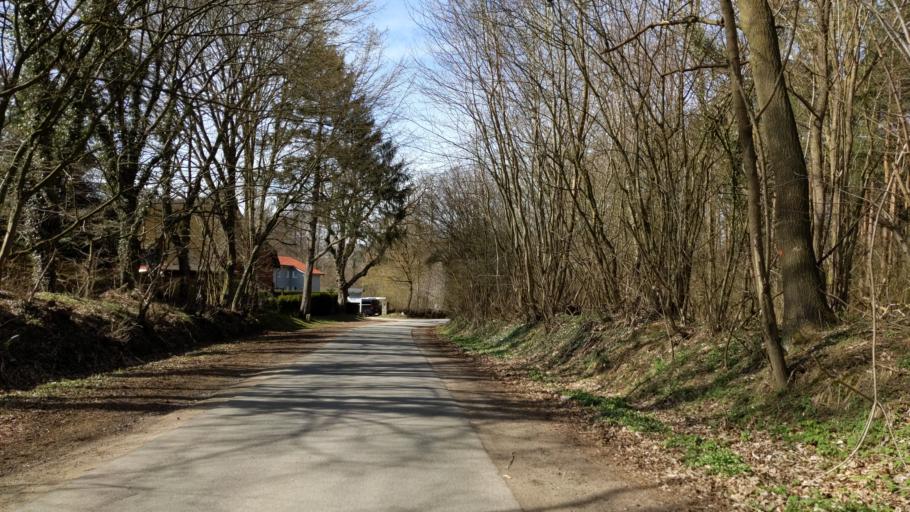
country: DE
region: Schleswig-Holstein
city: Ratekau
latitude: 53.9809
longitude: 10.6837
